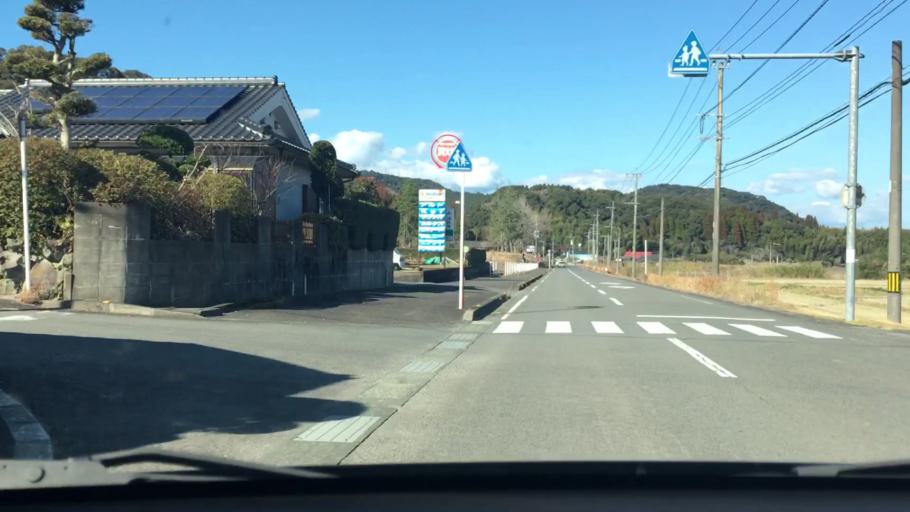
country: JP
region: Kagoshima
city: Satsumasendai
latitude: 31.7749
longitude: 130.4012
